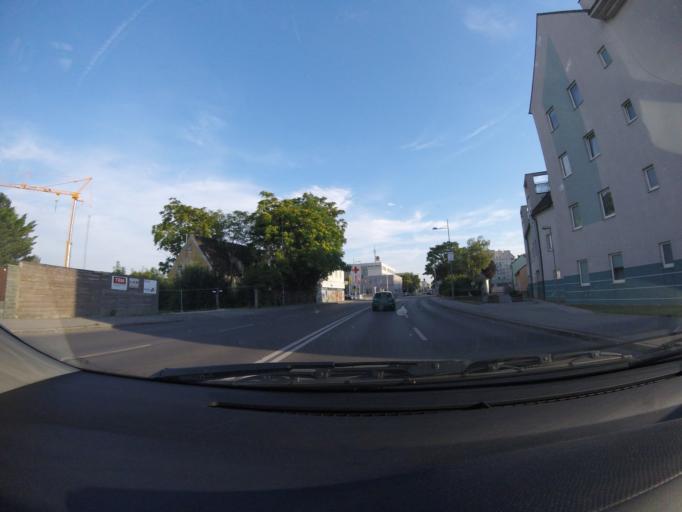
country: AT
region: Lower Austria
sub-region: Wiener Neustadt Stadt
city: Wiener Neustadt
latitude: 47.8198
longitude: 16.2482
